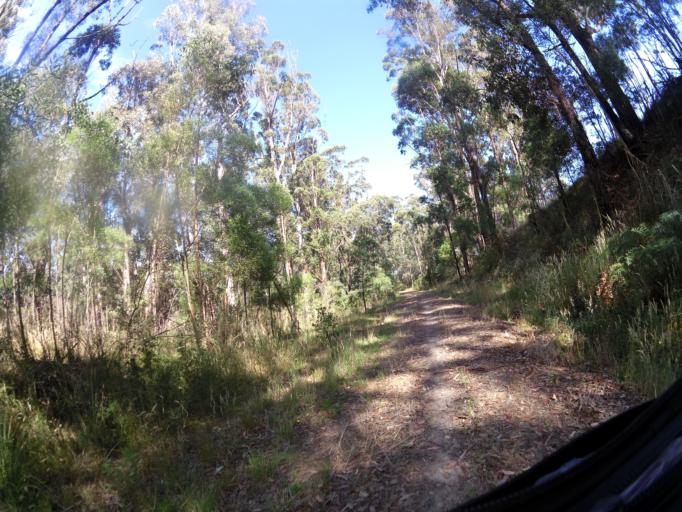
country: AU
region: Victoria
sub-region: East Gippsland
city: Lakes Entrance
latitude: -37.7506
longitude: 148.1870
